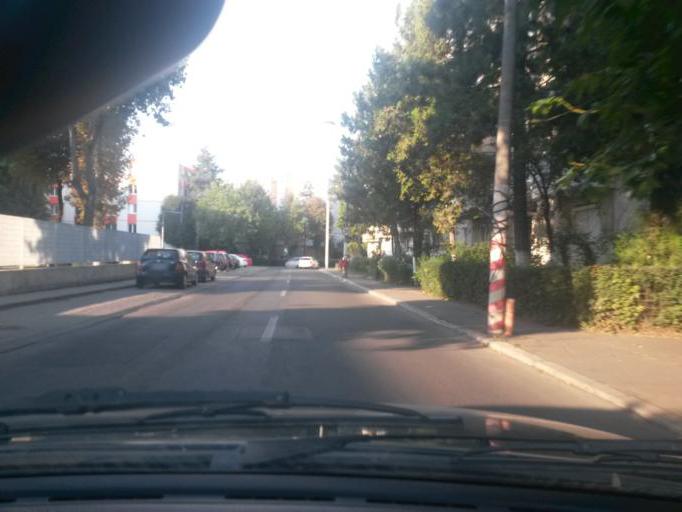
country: RO
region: Mures
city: Targu-Mures
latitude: 46.5342
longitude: 24.5621
